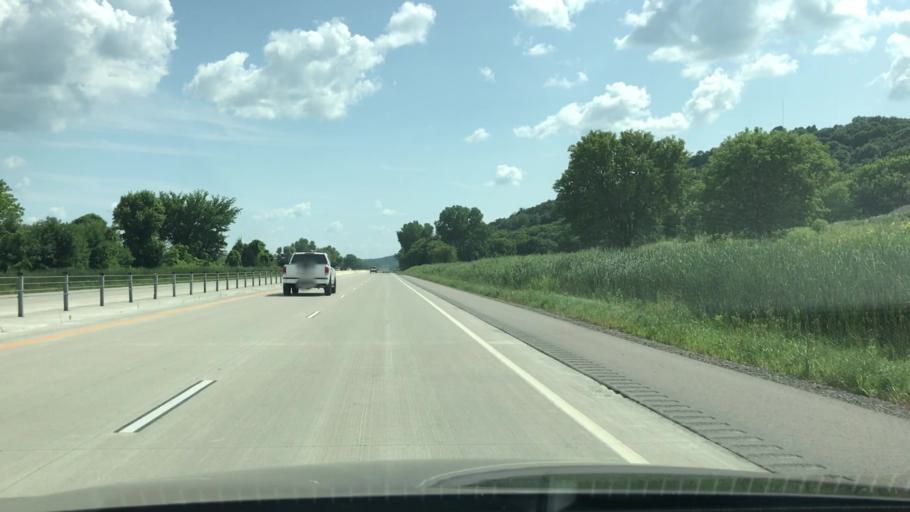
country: US
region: Minnesota
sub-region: Nicollet County
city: North Mankato
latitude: 44.2496
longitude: -94.0276
